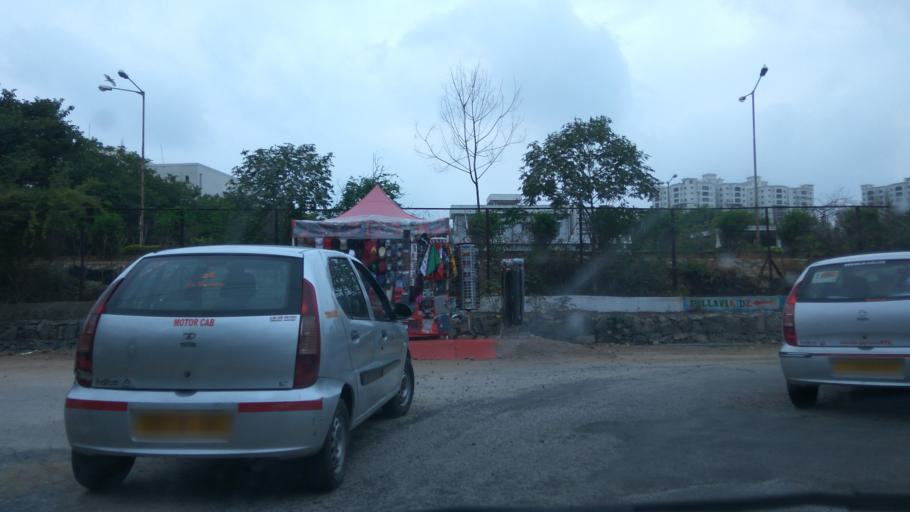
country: IN
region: Telangana
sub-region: Rangareddi
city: Kukatpalli
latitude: 17.4364
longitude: 78.3928
